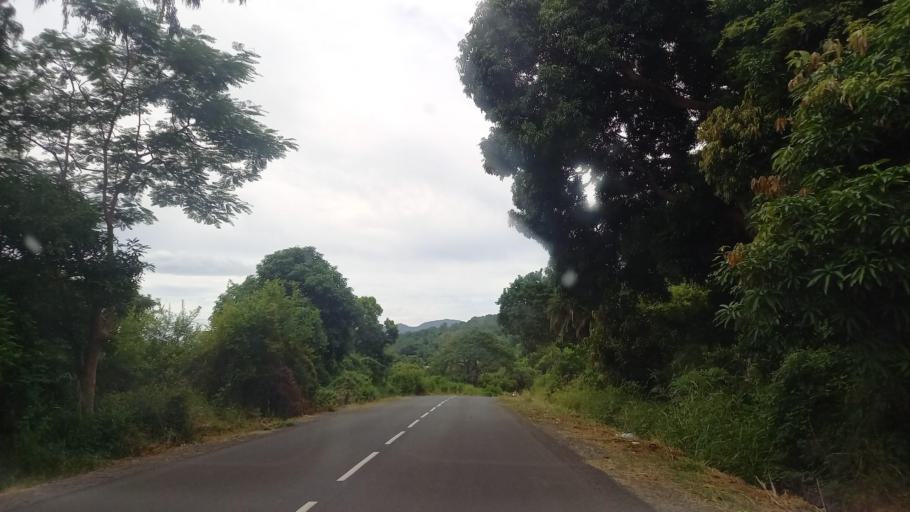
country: YT
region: Kani-Keli
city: Kani Keli
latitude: -12.9487
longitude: 45.0991
